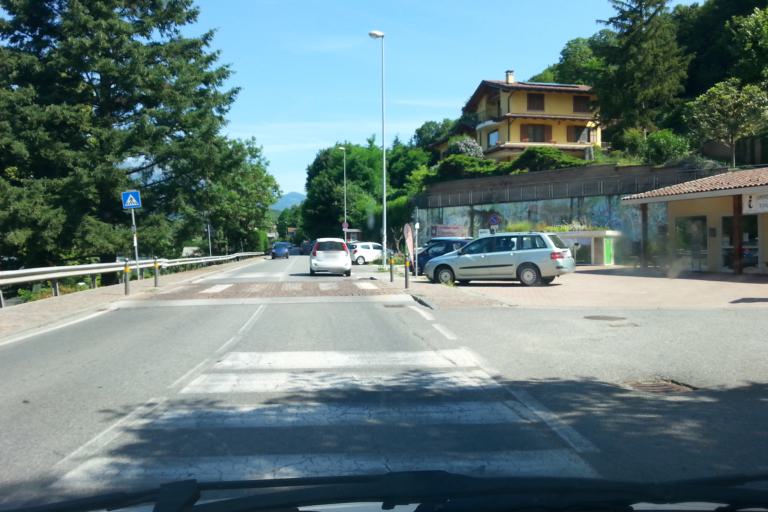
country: IT
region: Piedmont
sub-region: Provincia di Torino
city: Avigliana
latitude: 45.0650
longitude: 7.3933
